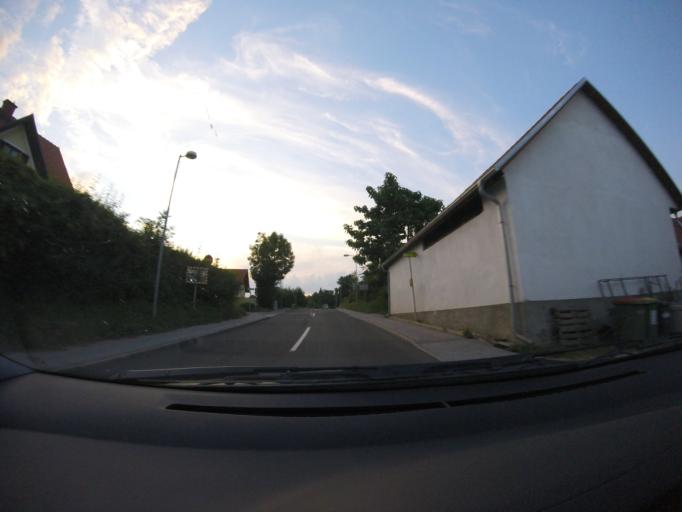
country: AT
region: Styria
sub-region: Politischer Bezirk Graz-Umgebung
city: Hart bei Graz
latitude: 47.0637
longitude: 15.5184
